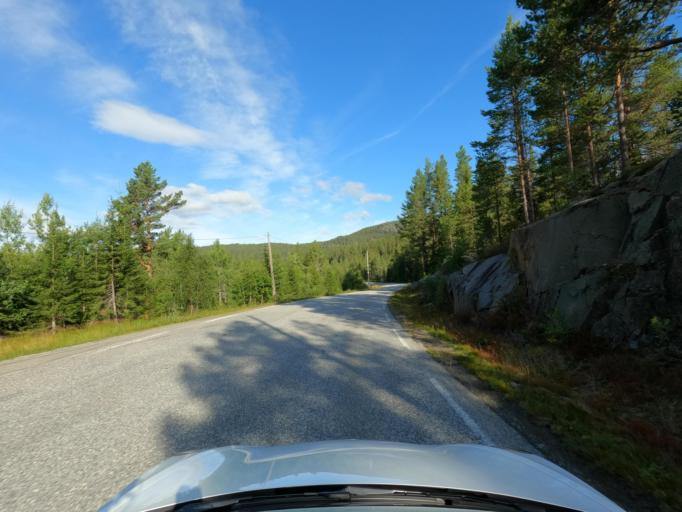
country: NO
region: Telemark
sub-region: Hjartdal
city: Sauland
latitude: 59.9231
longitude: 8.9726
